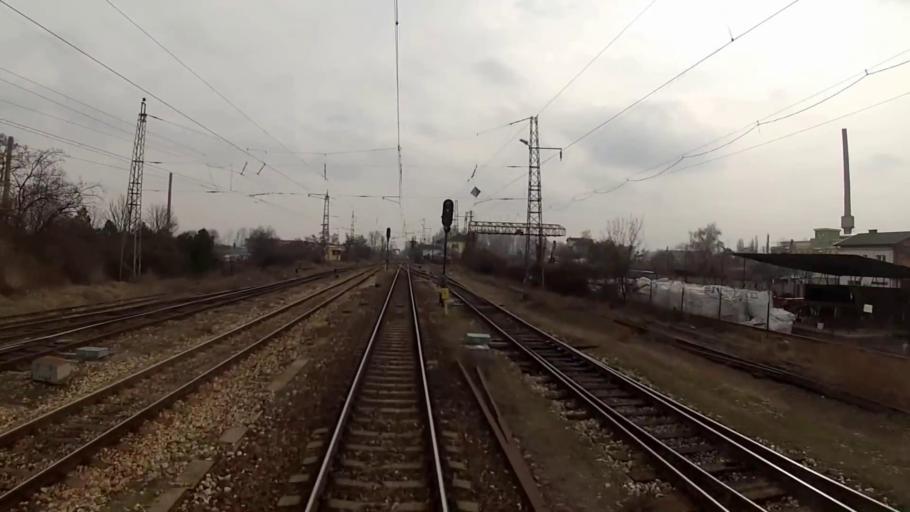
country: BG
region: Sofiya
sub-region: Obshtina Elin Pelin
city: Elin Pelin
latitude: 42.6544
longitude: 23.4599
